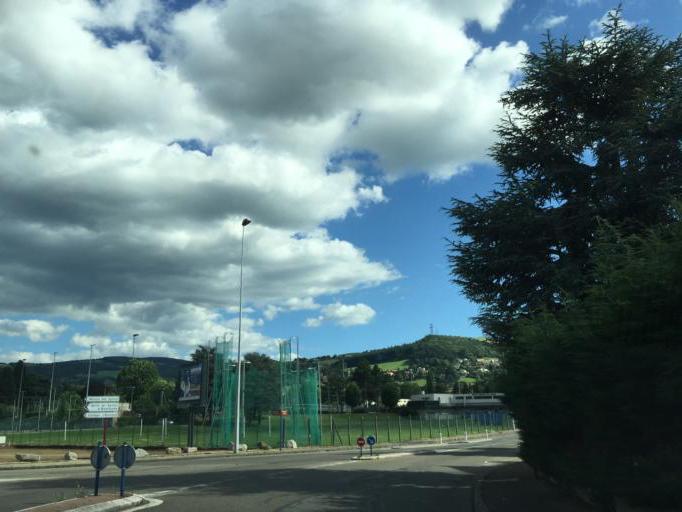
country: FR
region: Rhone-Alpes
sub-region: Departement de la Loire
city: Saint-Chamond
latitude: 45.4727
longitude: 4.5298
